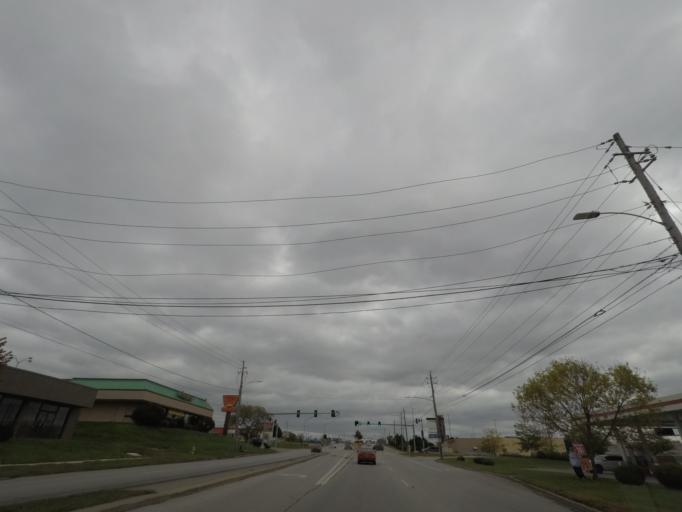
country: US
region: Iowa
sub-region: Polk County
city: Des Moines
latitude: 41.5263
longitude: -93.6015
